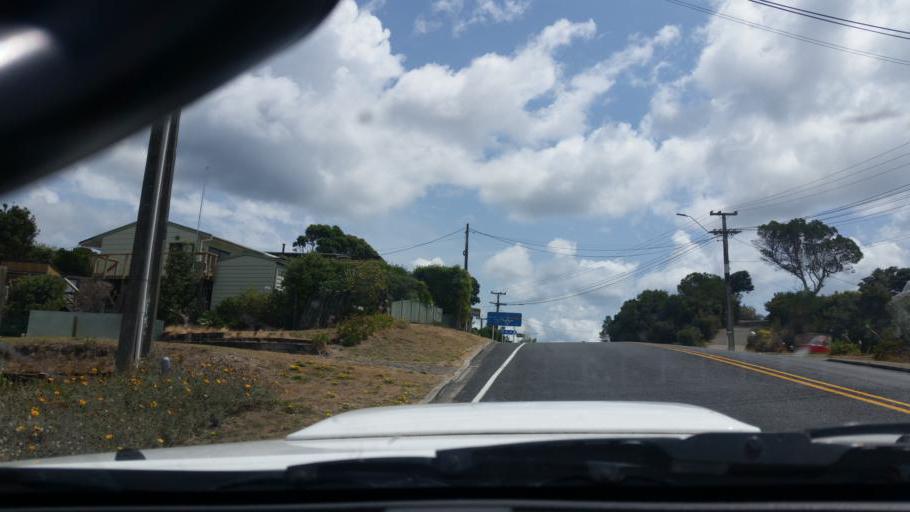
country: NZ
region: Auckland
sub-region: Auckland
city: Wellsford
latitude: -36.0883
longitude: 174.5833
